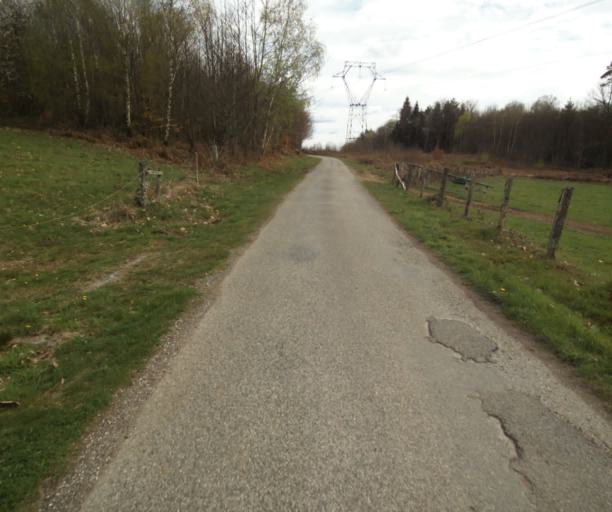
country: FR
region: Limousin
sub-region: Departement de la Correze
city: Argentat
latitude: 45.1886
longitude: 1.9143
